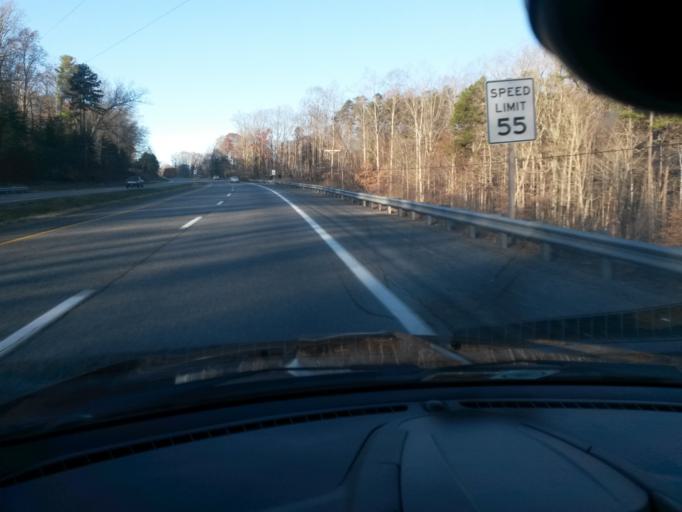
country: US
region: Virginia
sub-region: Henry County
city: Horse Pasture
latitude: 36.6198
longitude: -80.0121
